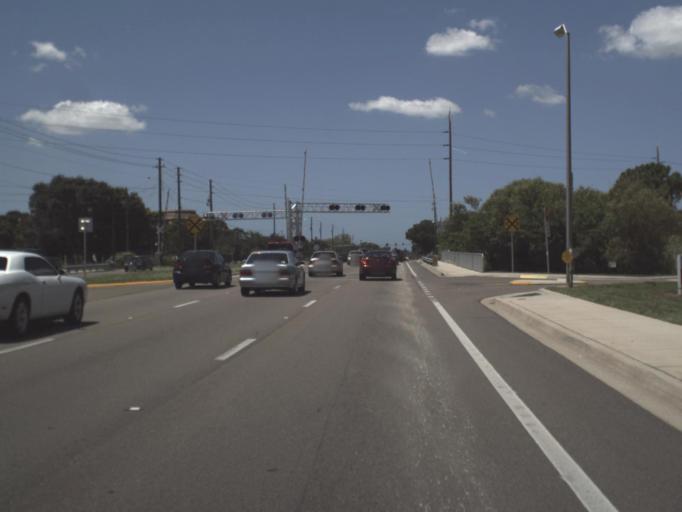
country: US
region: Florida
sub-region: Pinellas County
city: Seminole
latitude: 27.8724
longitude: -82.7488
